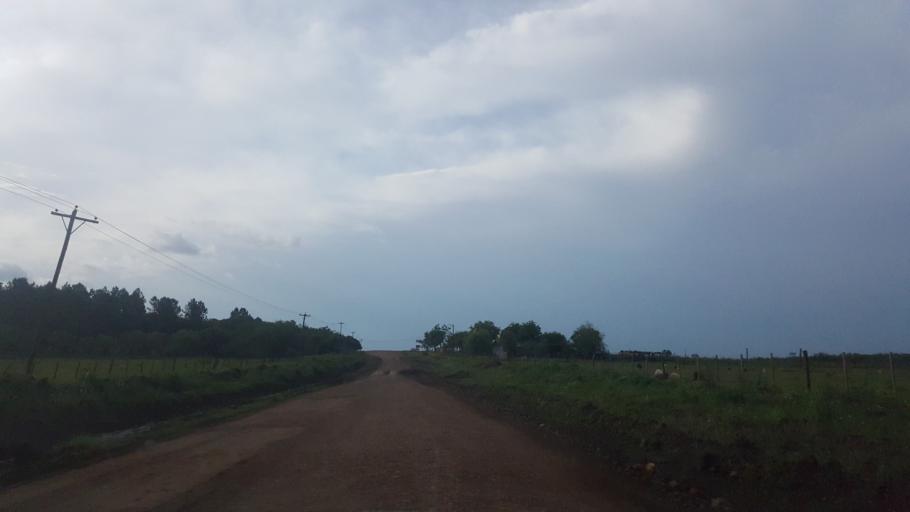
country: AR
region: Misiones
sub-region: Departamento de Candelaria
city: Candelaria
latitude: -27.5341
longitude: -55.7177
